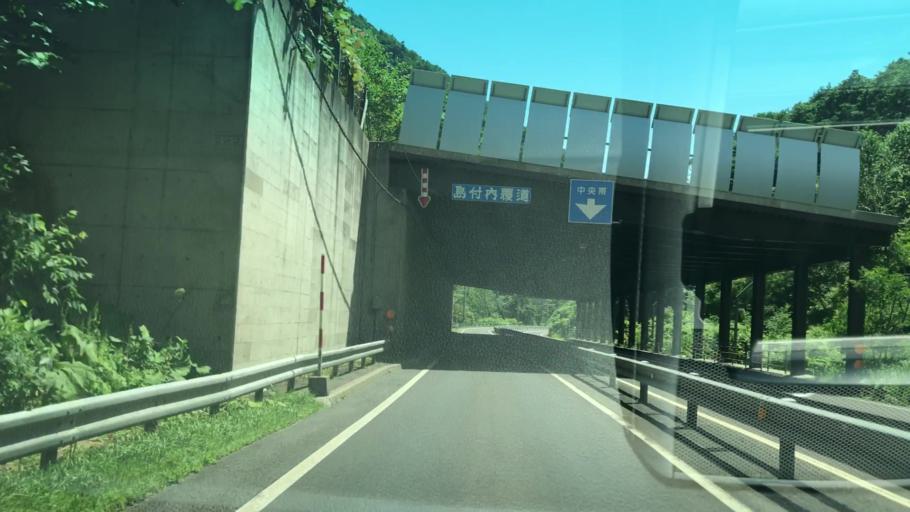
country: JP
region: Hokkaido
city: Yoichi
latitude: 43.0462
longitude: 140.6812
